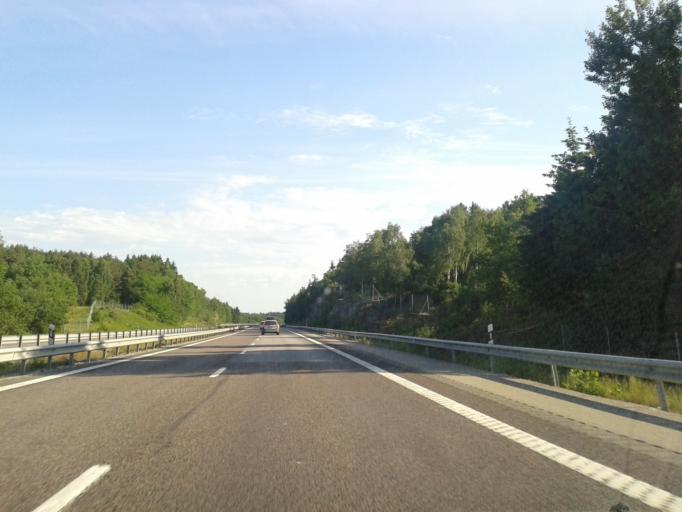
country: SE
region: Vaestra Goetaland
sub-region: Stenungsunds Kommun
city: Stora Hoga
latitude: 57.9889
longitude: 11.8425
